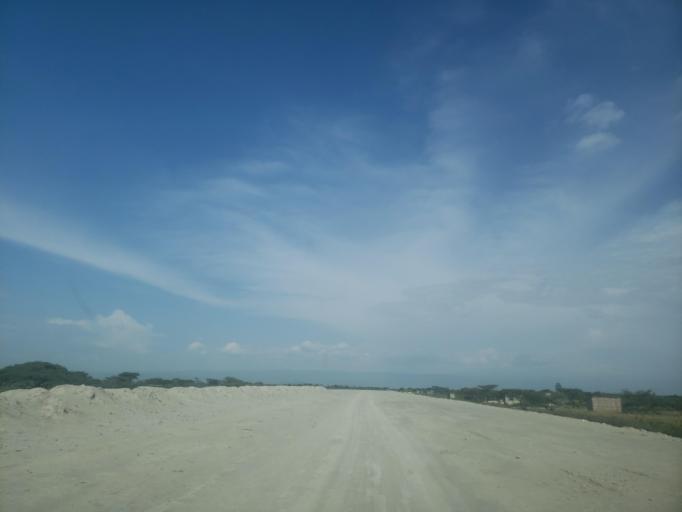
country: ET
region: Oromiya
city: Ziway
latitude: 7.6923
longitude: 38.6550
